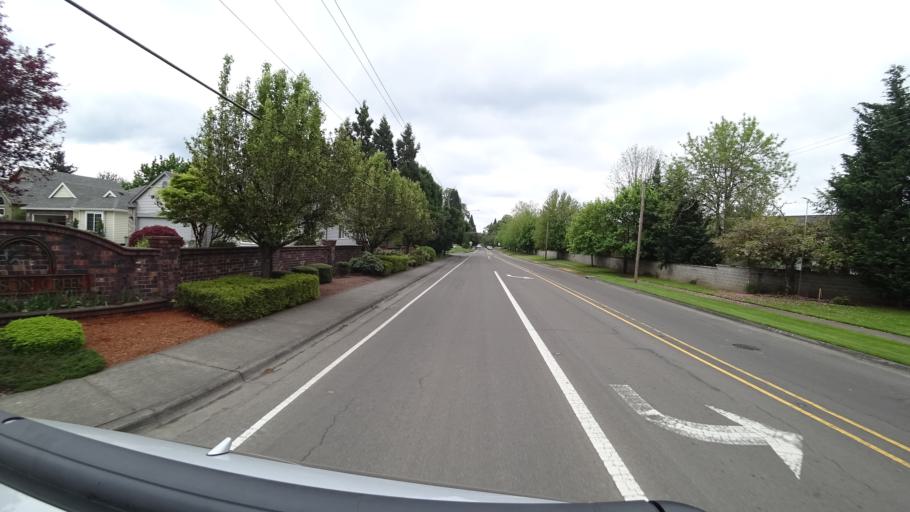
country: US
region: Oregon
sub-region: Washington County
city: Hillsboro
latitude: 45.5390
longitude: -122.9796
